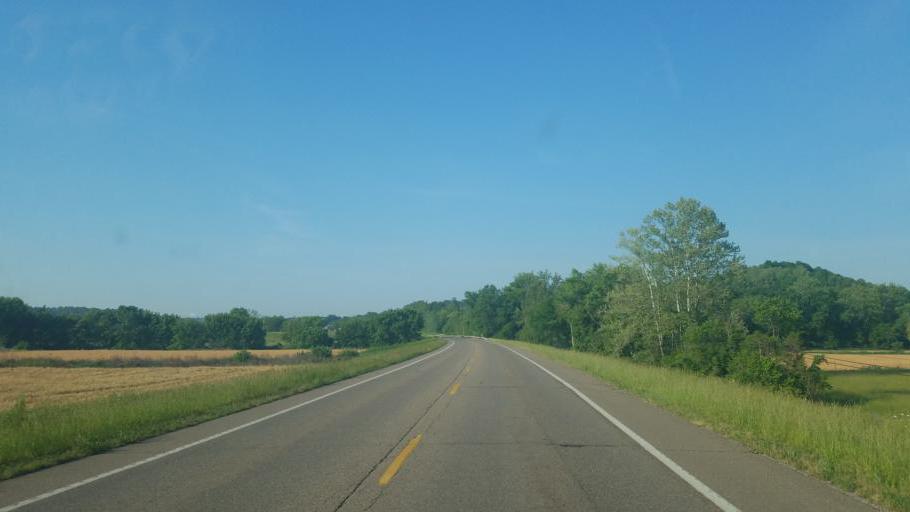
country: US
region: West Virginia
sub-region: Mason County
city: New Haven
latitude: 39.1025
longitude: -81.9245
